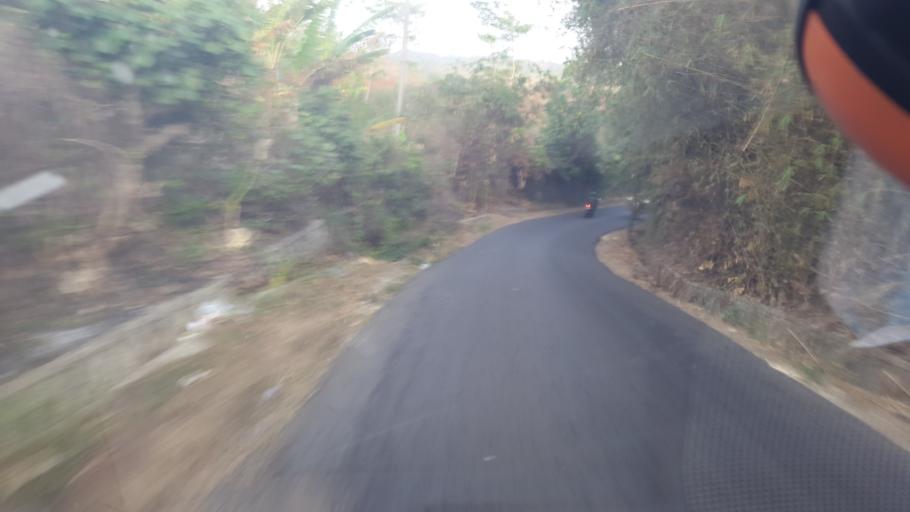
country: ID
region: West Java
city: Pondokaso
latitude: -7.3532
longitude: 106.5359
